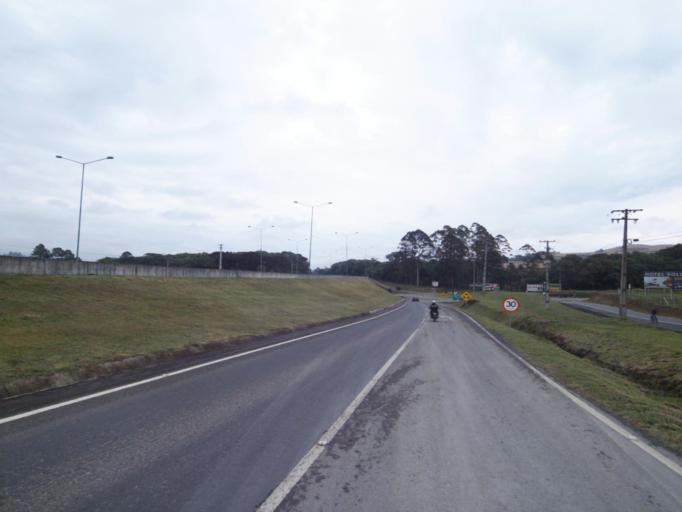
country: BR
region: Parana
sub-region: Irati
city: Irati
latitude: -25.4537
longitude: -50.6174
